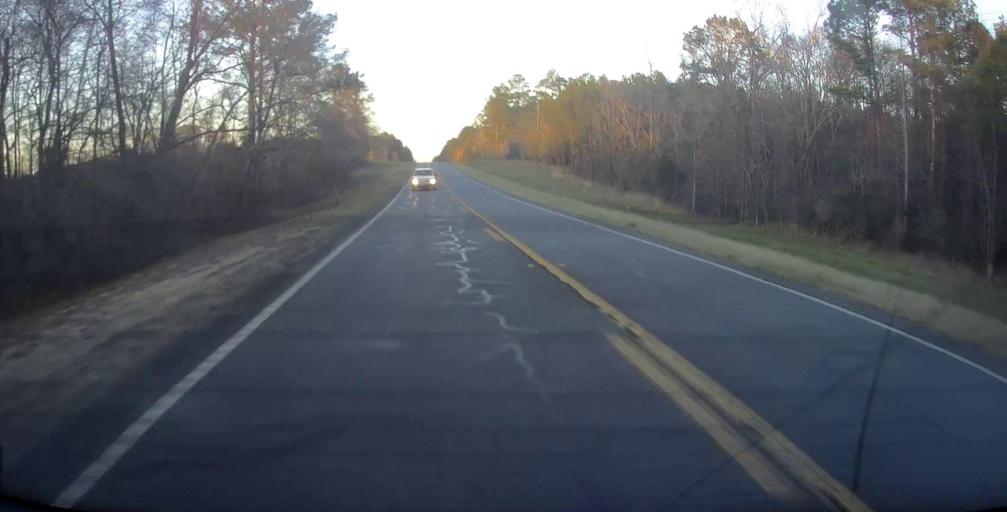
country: US
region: Georgia
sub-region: Dodge County
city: Eastman
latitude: 32.2254
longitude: -83.1544
